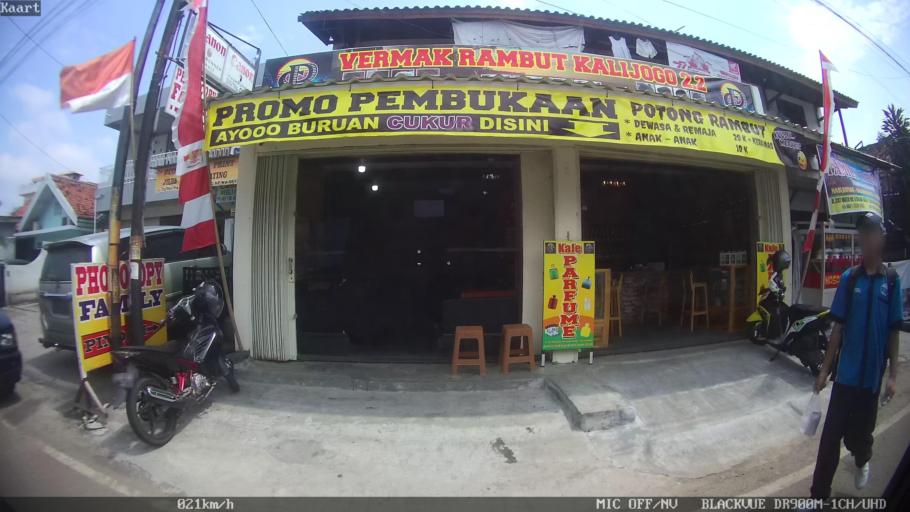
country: ID
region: Lampung
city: Bandarlampung
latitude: -5.4340
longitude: 105.2620
